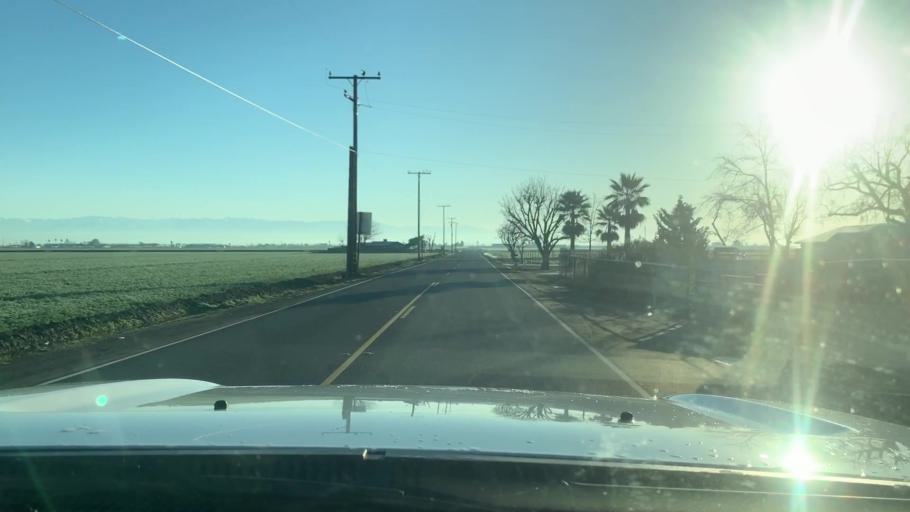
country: US
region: California
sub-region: Kings County
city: Corcoran
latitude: 36.2033
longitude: -119.4922
